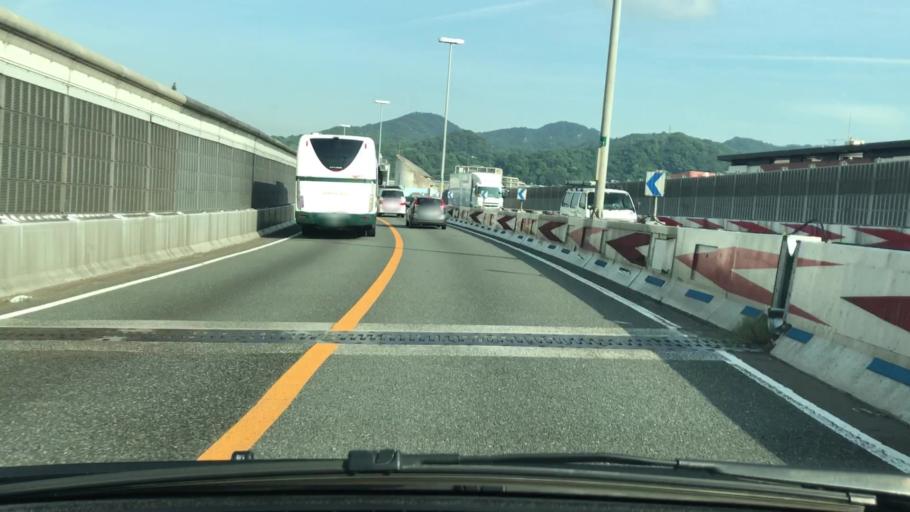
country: JP
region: Hyogo
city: Kobe
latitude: 34.6499
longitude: 135.1301
